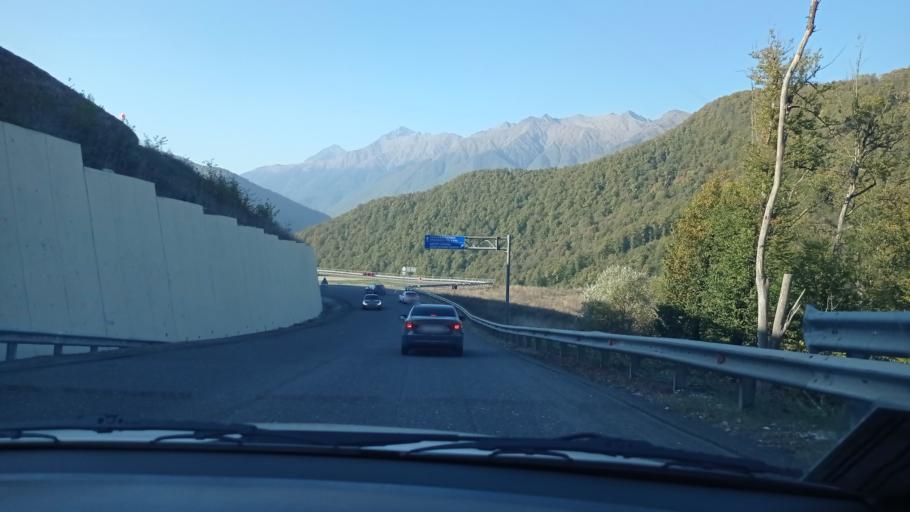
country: RU
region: Krasnodarskiy
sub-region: Sochi City
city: Krasnaya Polyana
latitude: 43.6699
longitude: 40.2898
